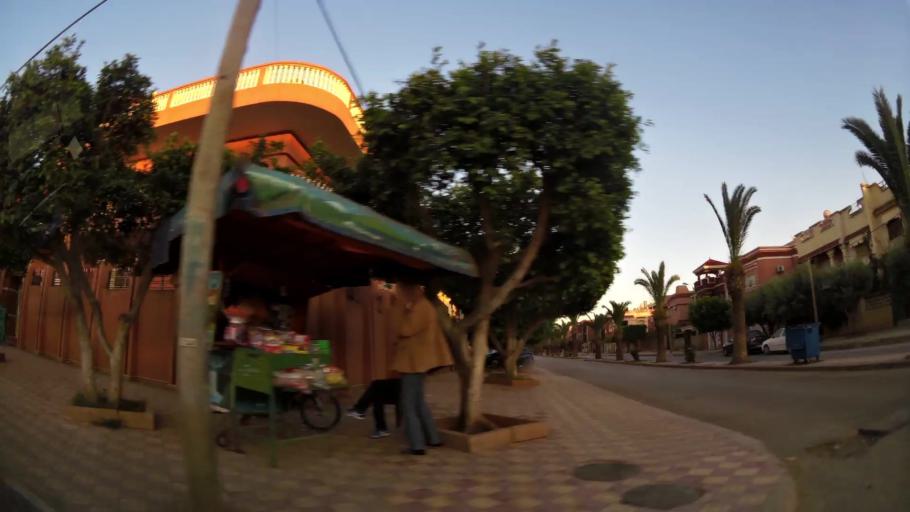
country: MA
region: Oriental
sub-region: Berkane-Taourirt
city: Berkane
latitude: 34.9153
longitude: -2.3165
